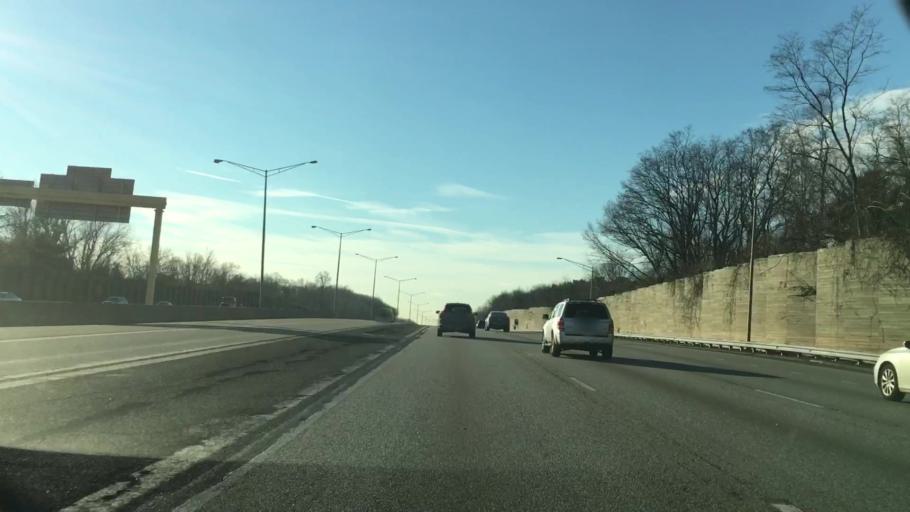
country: US
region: Connecticut
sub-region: Hartford County
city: Windsor
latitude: 41.8487
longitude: -72.6658
